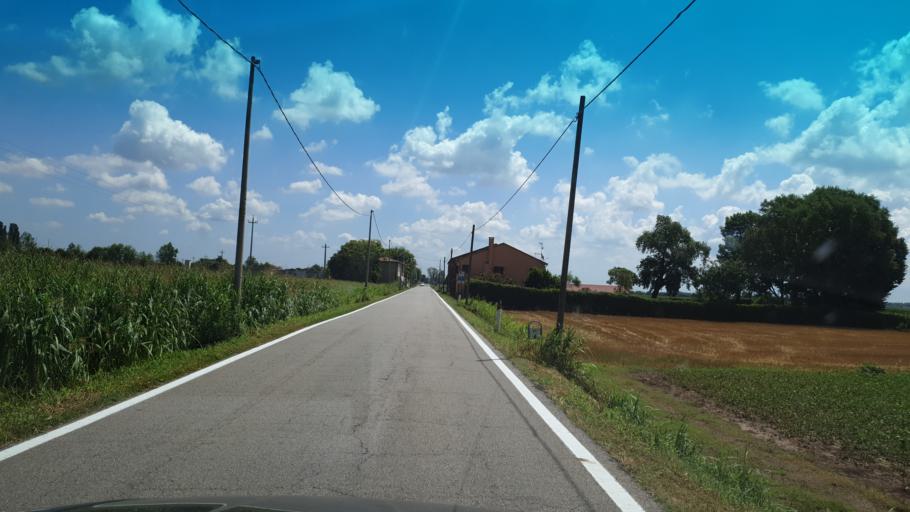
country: IT
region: Veneto
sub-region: Provincia di Rovigo
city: Mardimago
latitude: 45.1482
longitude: 11.8138
